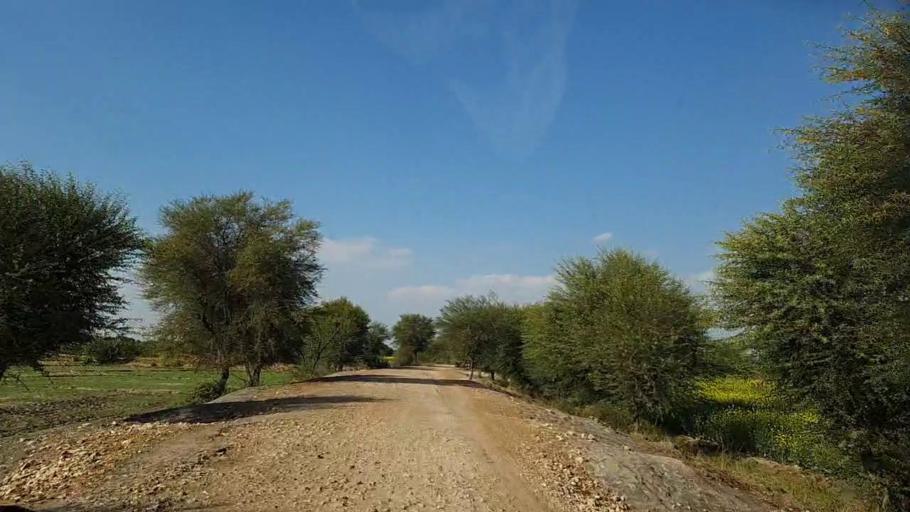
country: PK
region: Sindh
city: Pithoro
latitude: 25.6281
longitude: 69.3521
